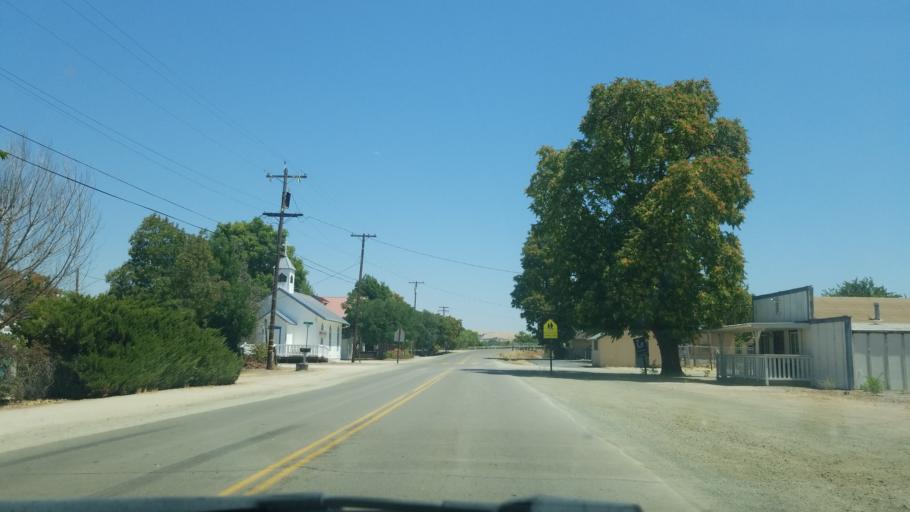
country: US
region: California
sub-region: San Luis Obispo County
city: Atascadero
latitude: 35.5190
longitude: -120.5235
